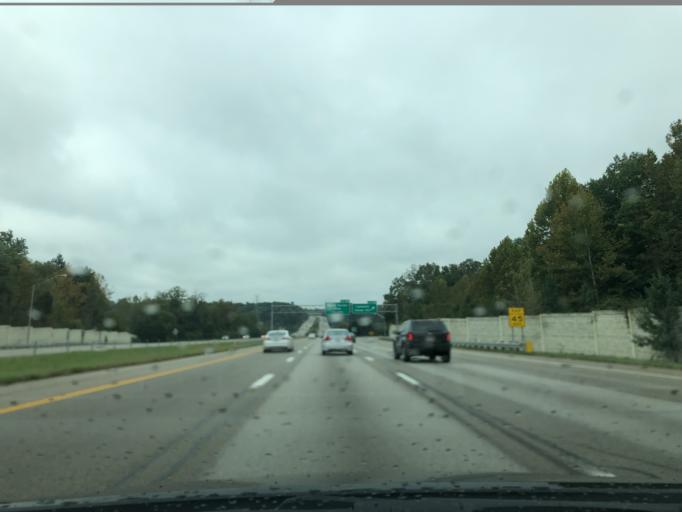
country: US
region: Ohio
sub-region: Hamilton County
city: The Village of Indian Hill
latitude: 39.2460
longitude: -84.3043
